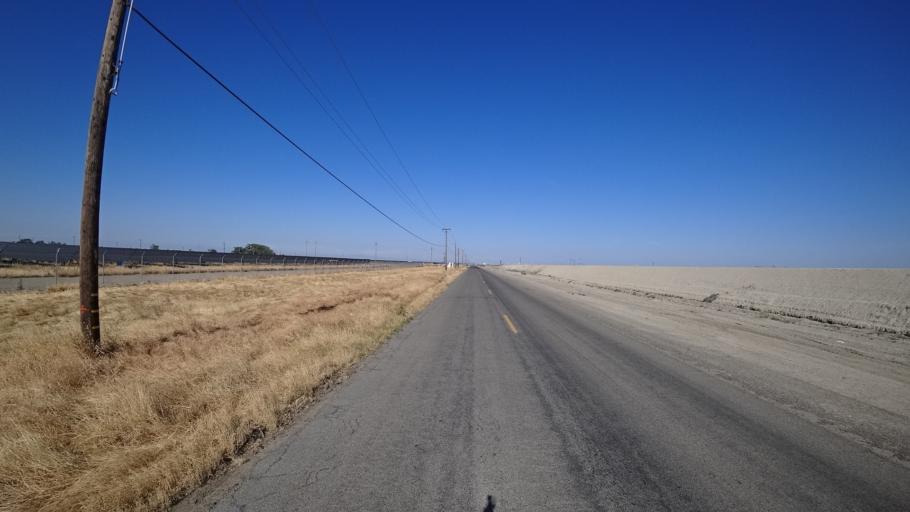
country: US
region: California
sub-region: Kings County
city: Corcoran
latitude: 36.1379
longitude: -119.5610
